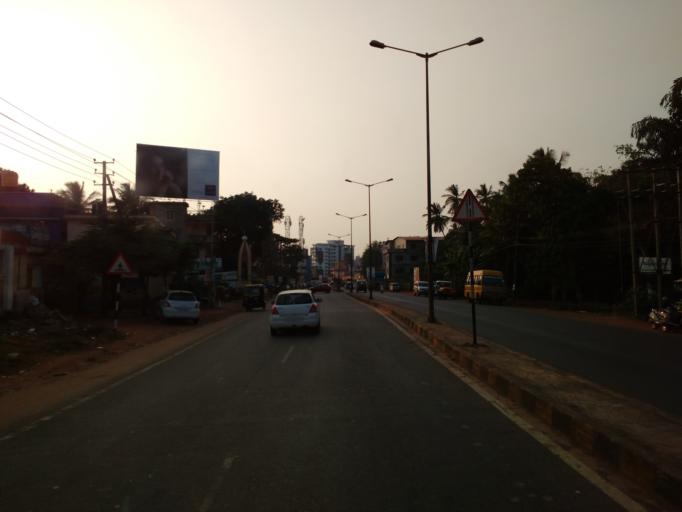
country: IN
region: Karnataka
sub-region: Dakshina Kannada
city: Mangalore
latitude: 12.8835
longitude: 74.8704
